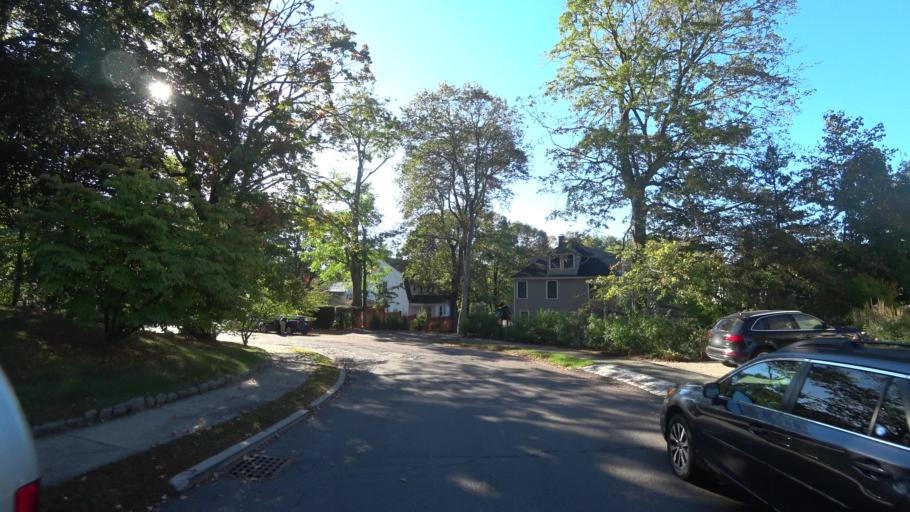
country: US
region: Massachusetts
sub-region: Middlesex County
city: Newton
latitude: 42.3356
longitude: -71.2021
